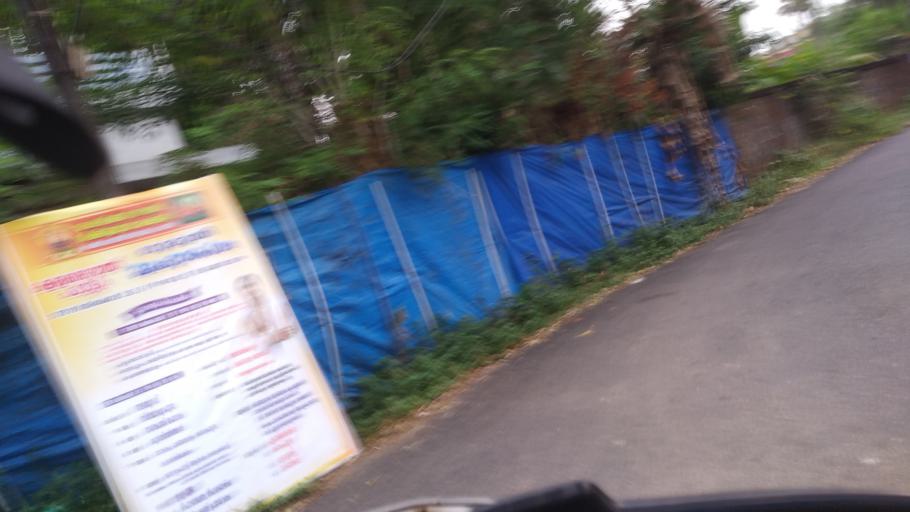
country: IN
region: Kerala
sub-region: Thrissur District
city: Kodungallur
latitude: 10.1376
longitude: 76.2004
